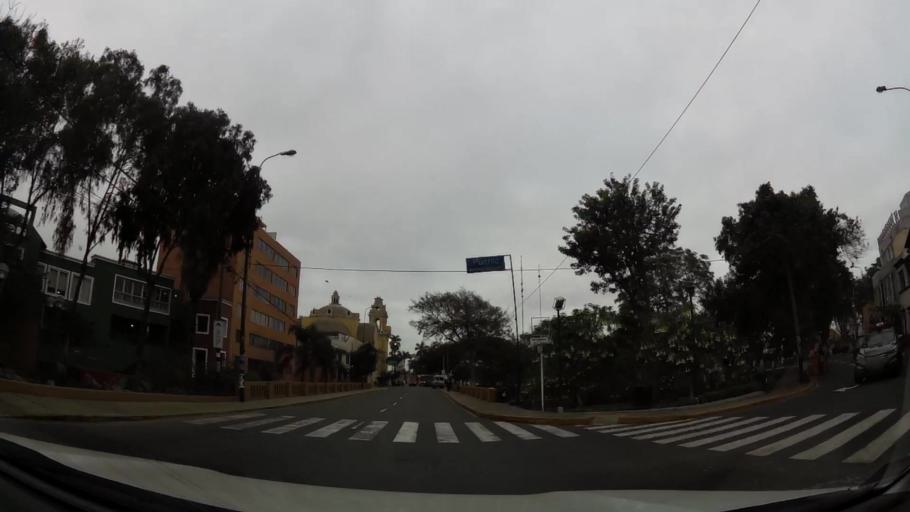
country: PE
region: Lima
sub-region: Lima
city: Surco
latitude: -12.1478
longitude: -77.0222
